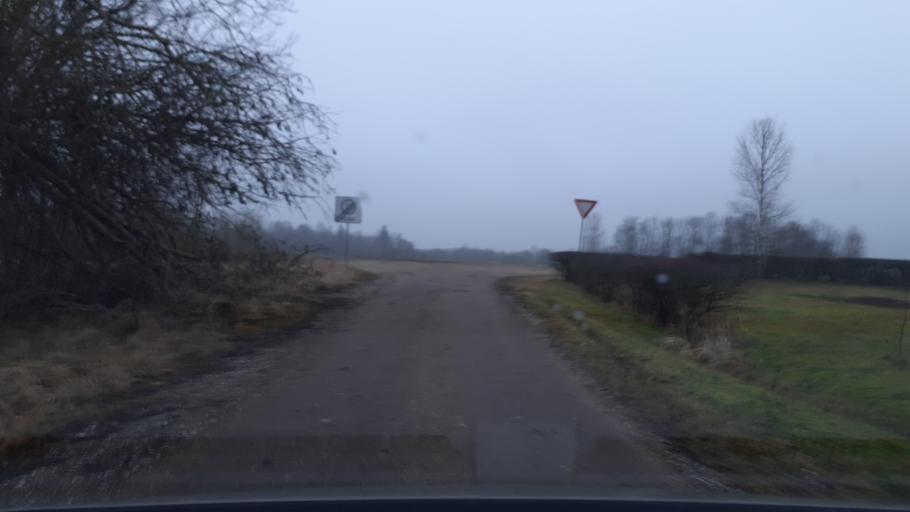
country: LV
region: Talsu Rajons
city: Sabile
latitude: 56.9559
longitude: 22.3992
